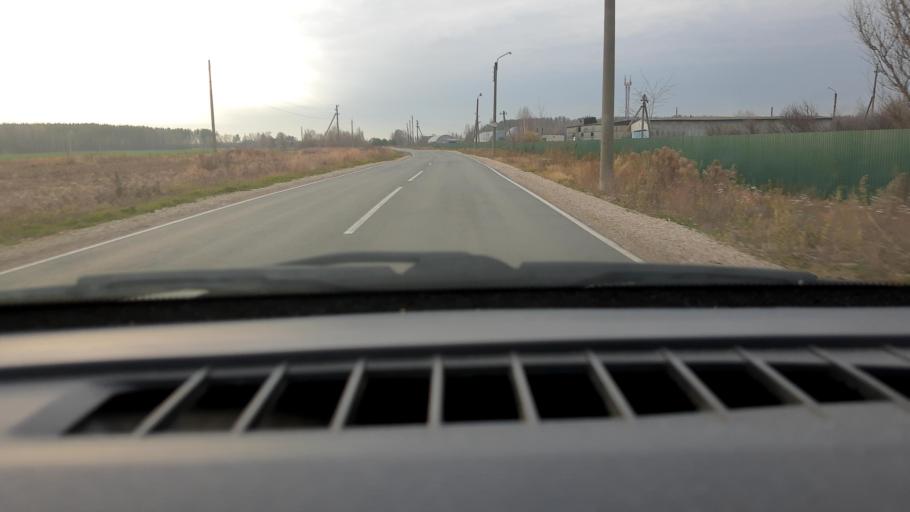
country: RU
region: Nizjnij Novgorod
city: Neklyudovo
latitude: 56.4465
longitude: 43.8992
